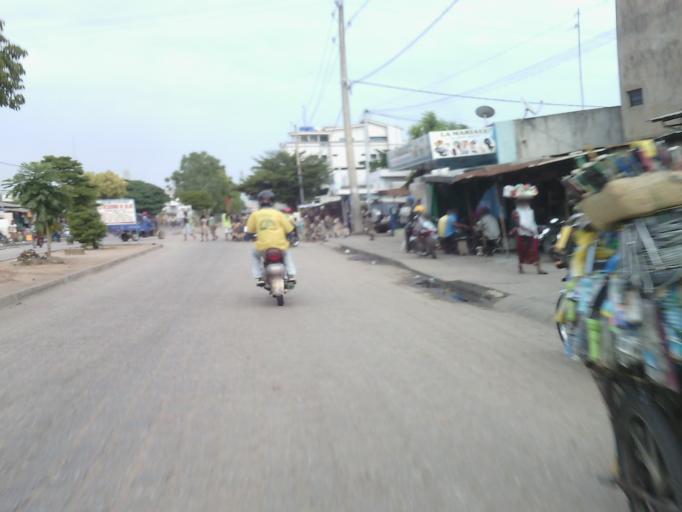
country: BJ
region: Littoral
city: Cotonou
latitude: 6.3896
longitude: 2.3724
